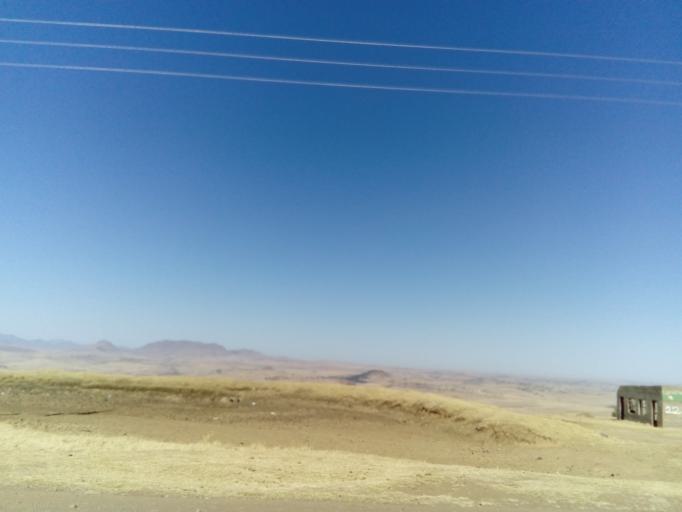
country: LS
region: Berea
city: Teyateyaneng
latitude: -29.1316
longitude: 27.8432
